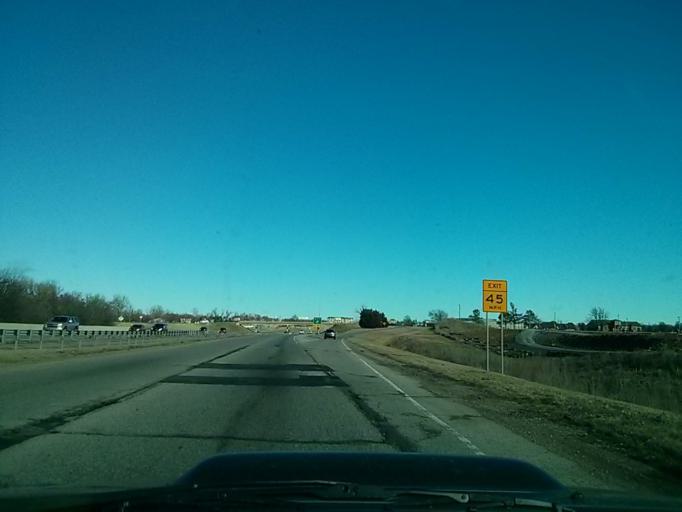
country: US
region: Oklahoma
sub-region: Tulsa County
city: Jenks
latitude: 36.0215
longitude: -96.0115
